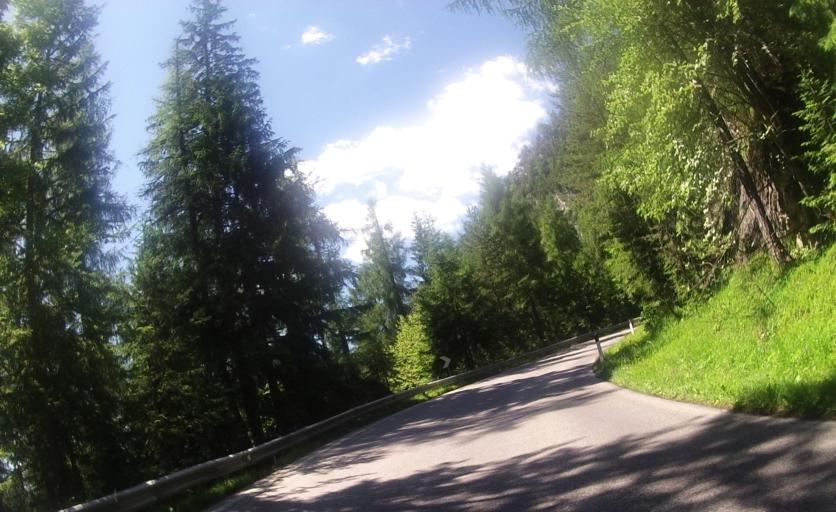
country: IT
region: Veneto
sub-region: Provincia di Belluno
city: Cortina d'Ampezzo
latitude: 46.5262
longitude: 12.1206
